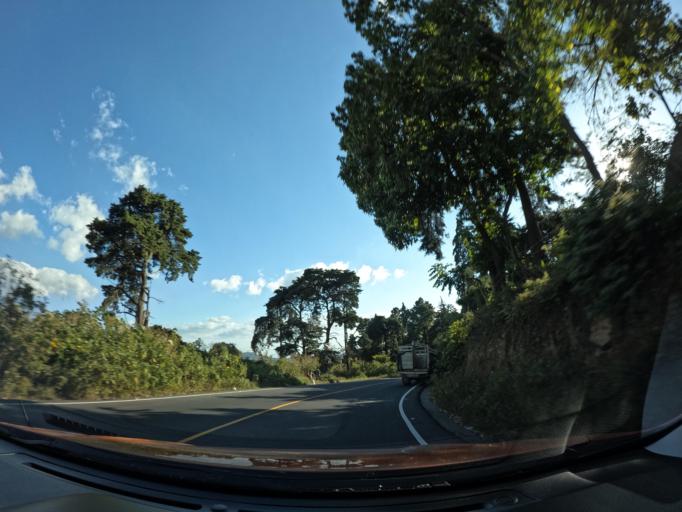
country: GT
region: Escuintla
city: Palin
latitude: 14.4486
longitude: -90.6924
